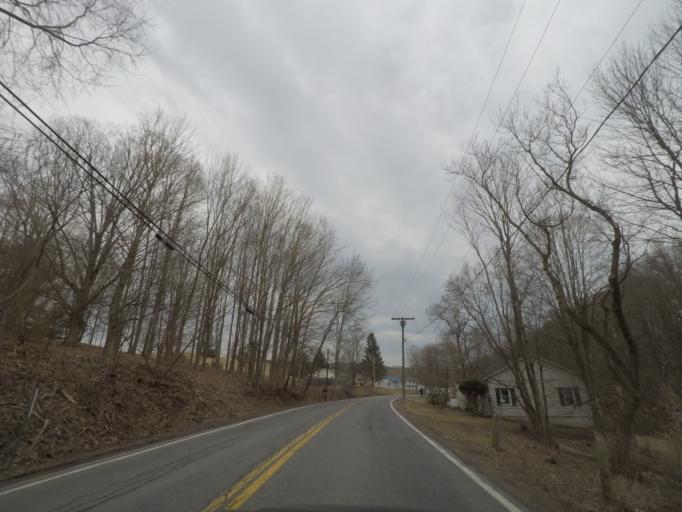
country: US
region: New York
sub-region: Washington County
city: Greenwich
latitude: 43.0792
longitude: -73.4958
